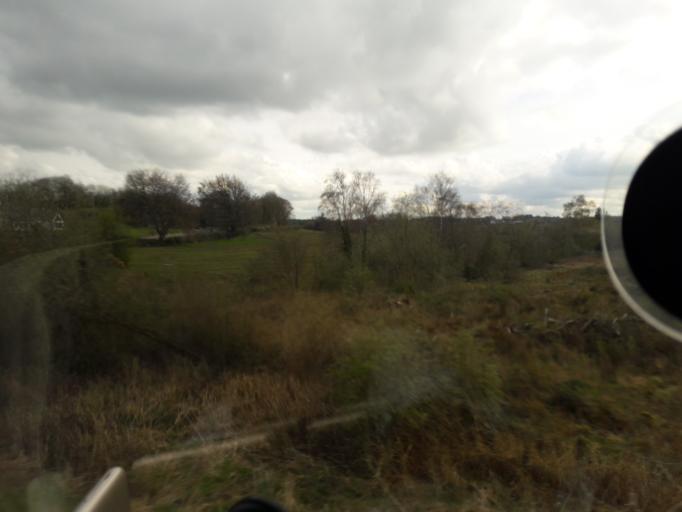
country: IE
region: Leinster
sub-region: An Iarmhi
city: Rochfortbridge
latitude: 53.4982
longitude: -7.2479
